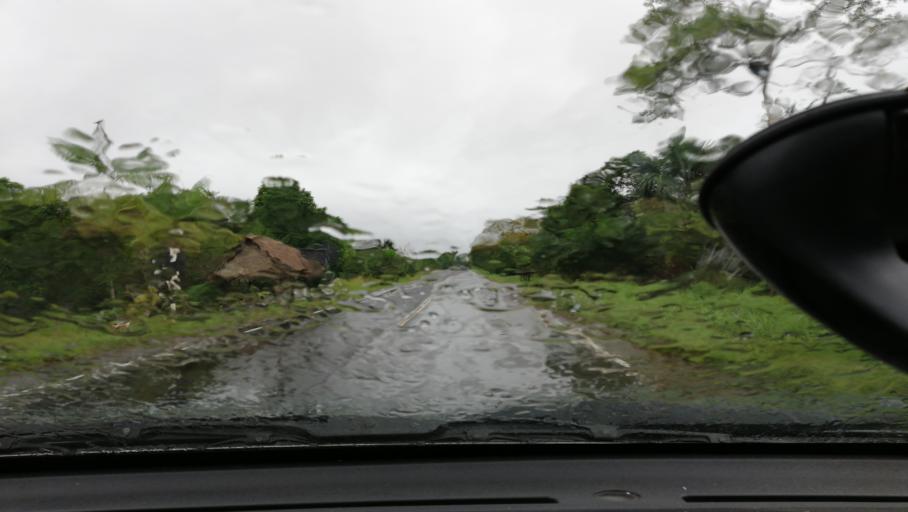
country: PE
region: Loreto
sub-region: Provincia de Maynas
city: San Juan
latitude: -4.1925
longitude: -73.4762
